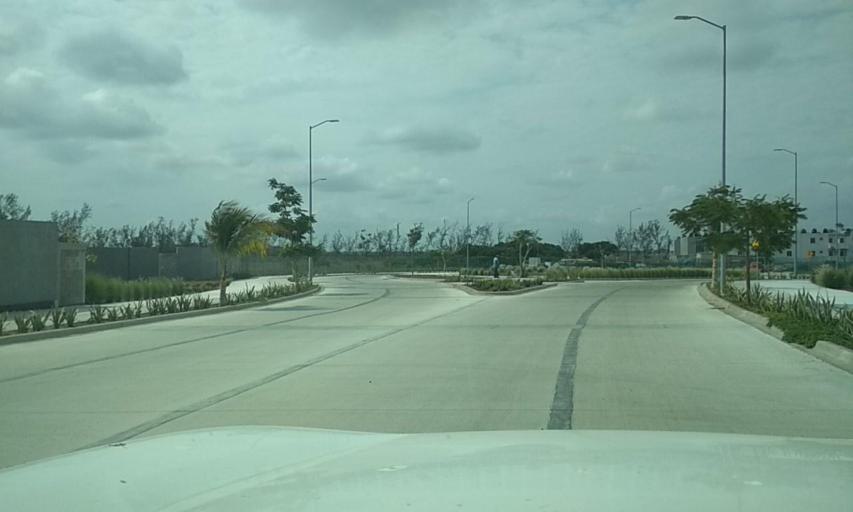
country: MX
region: Veracruz
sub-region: Veracruz
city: Las Amapolas
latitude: 19.1496
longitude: -96.2150
